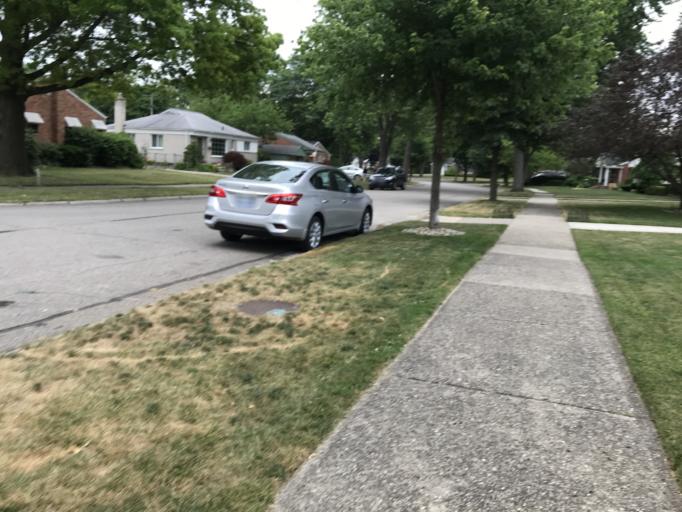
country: US
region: Michigan
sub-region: Oakland County
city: Farmington
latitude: 42.4682
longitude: -83.3615
